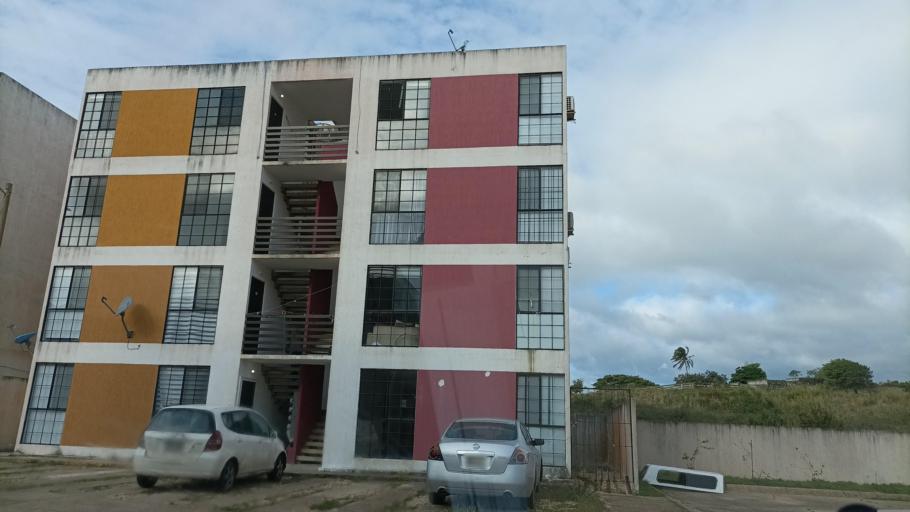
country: MX
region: Veracruz
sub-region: Coatzacoalcos
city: Fraccionamiento Ciudad Olmeca
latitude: 18.1569
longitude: -94.5595
